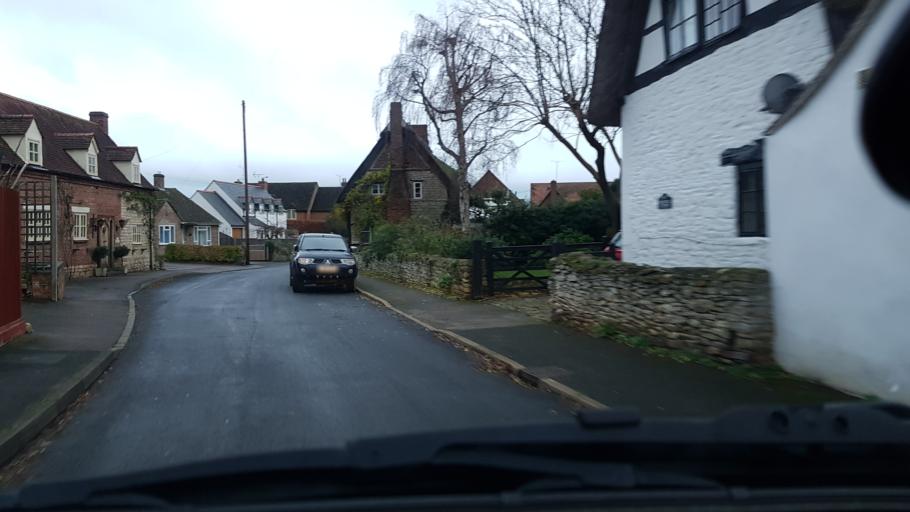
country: GB
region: England
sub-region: Gloucestershire
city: Winchcombe
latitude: 51.9981
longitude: -1.9993
